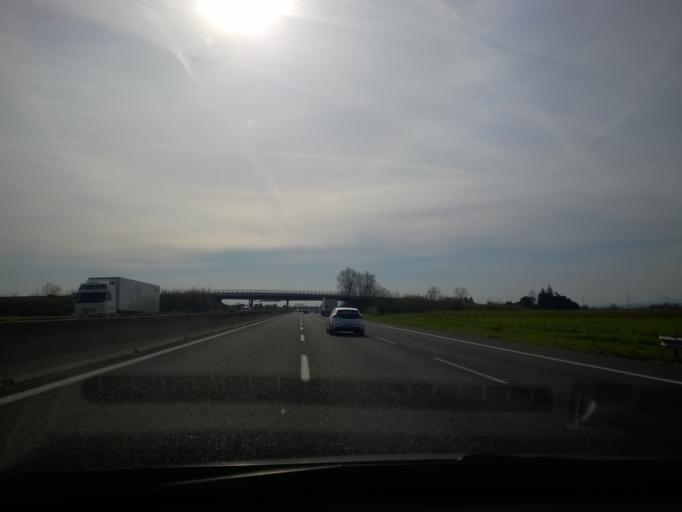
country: IT
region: Emilia-Romagna
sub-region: Forli-Cesena
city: Bagnarola
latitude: 44.1642
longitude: 12.2976
